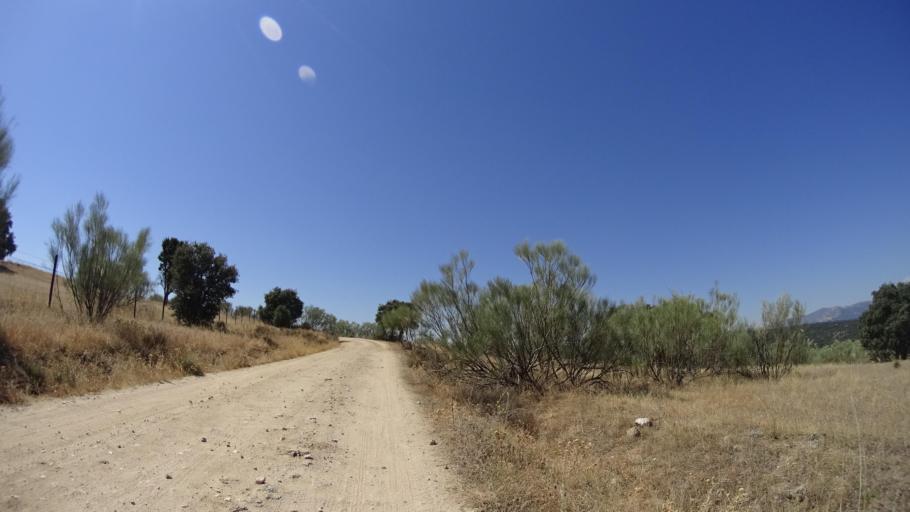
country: ES
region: Madrid
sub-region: Provincia de Madrid
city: Colmenarejo
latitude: 40.5182
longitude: -4.0133
